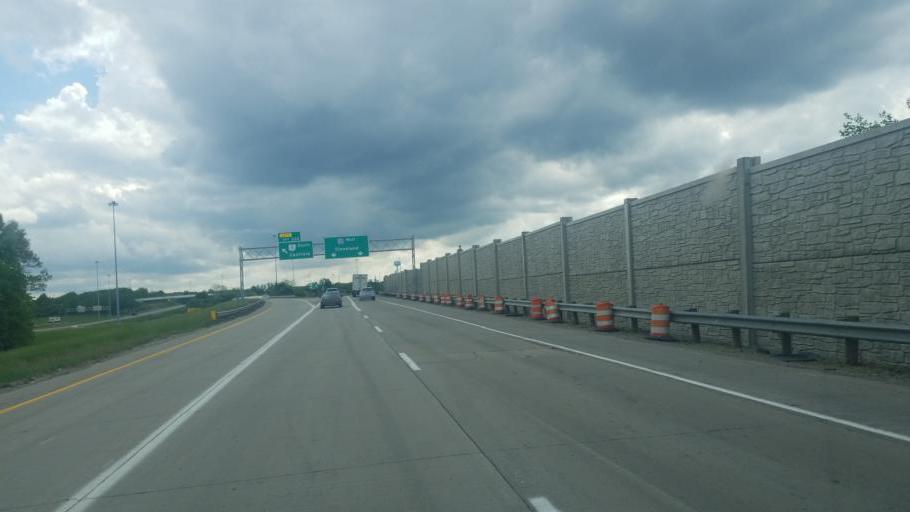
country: US
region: Ohio
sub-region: Trumbull County
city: Mineral Ridge
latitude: 41.1290
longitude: -80.7472
